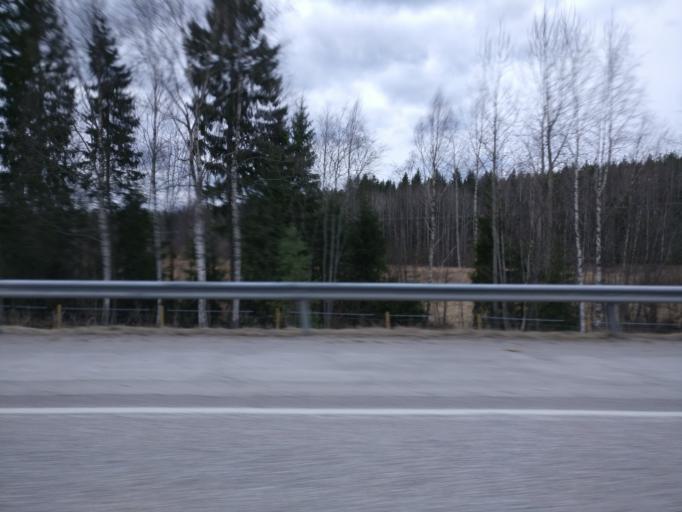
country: FI
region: Uusimaa
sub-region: Helsinki
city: Hyvinge
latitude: 60.6498
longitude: 24.8036
